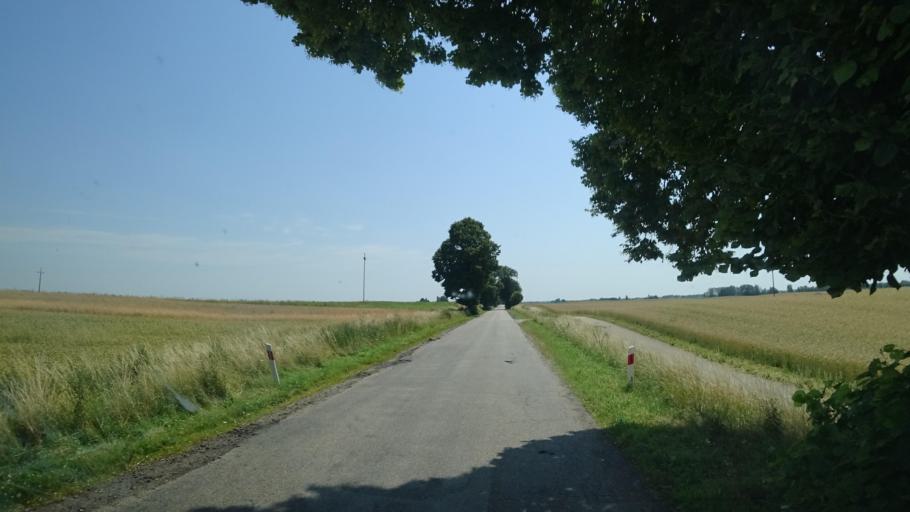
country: PL
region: Pomeranian Voivodeship
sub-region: Powiat chojnicki
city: Brusy
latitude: 53.8803
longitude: 17.6467
